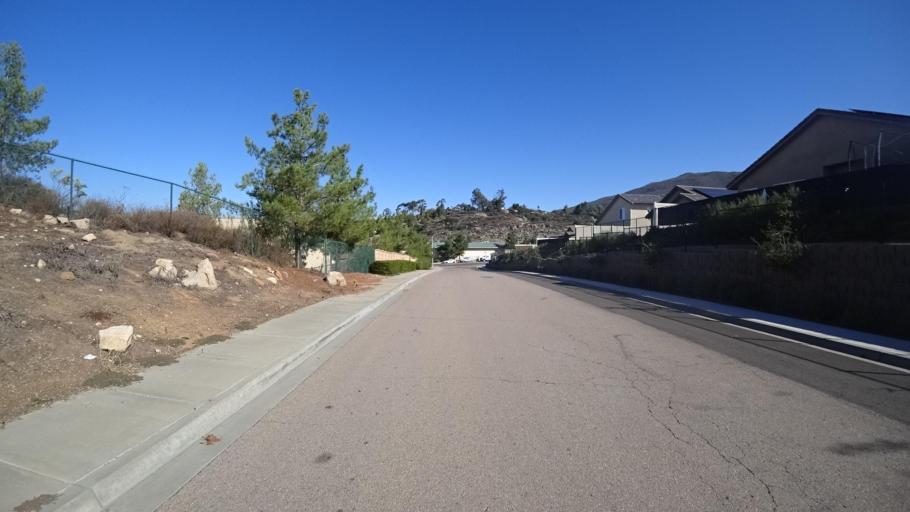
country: US
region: California
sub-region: San Diego County
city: Alpine
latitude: 32.8327
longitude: -116.7494
